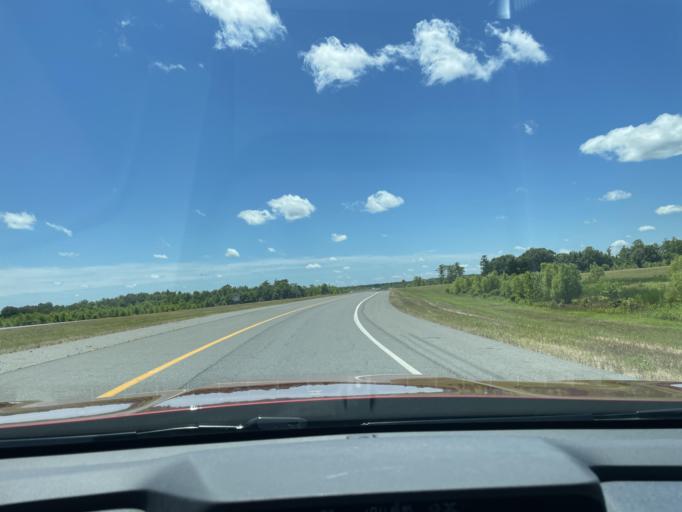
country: US
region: Arkansas
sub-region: Jefferson County
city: Pine Bluff
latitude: 34.1716
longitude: -91.9865
